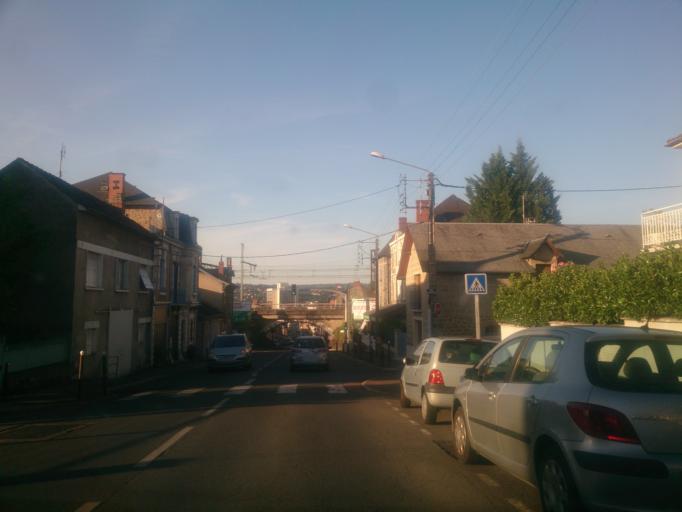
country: FR
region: Limousin
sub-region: Departement de la Correze
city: Brive-la-Gaillarde
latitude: 45.1500
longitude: 1.5314
